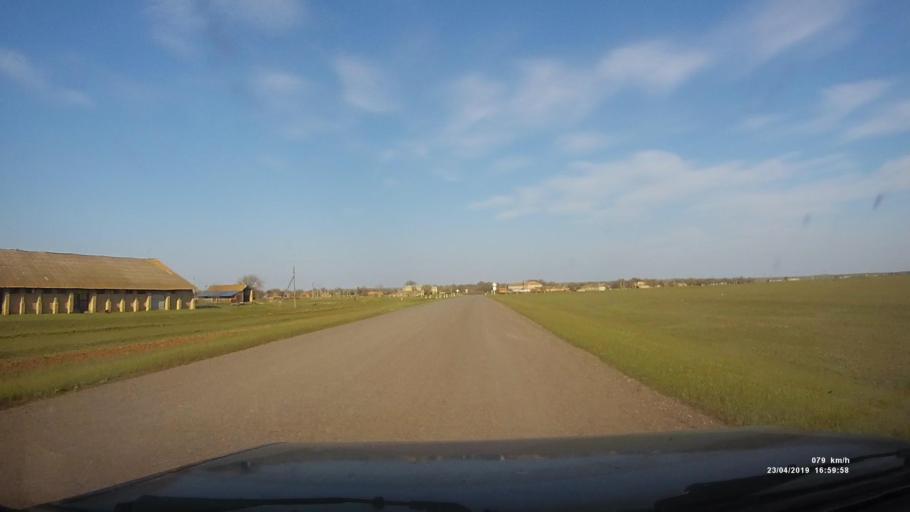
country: RU
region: Kalmykiya
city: Priyutnoye
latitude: 46.3084
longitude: 43.3997
